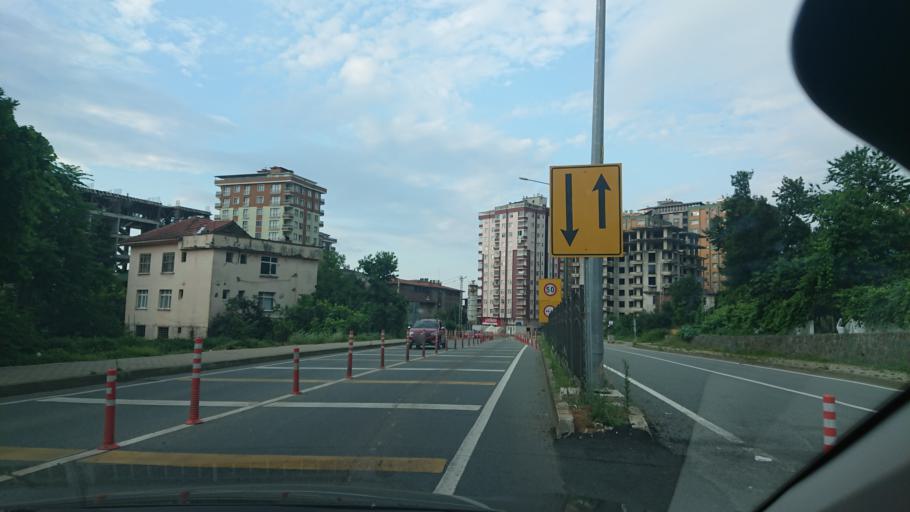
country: TR
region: Rize
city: Gundogdu
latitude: 41.0357
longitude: 40.5652
